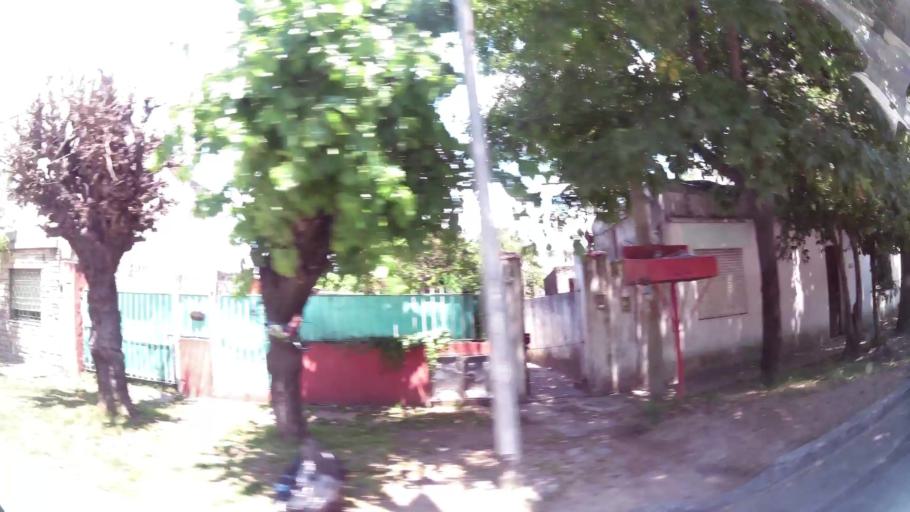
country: AR
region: Buenos Aires
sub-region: Partido de Tigre
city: Tigre
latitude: -34.4138
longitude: -58.6015
